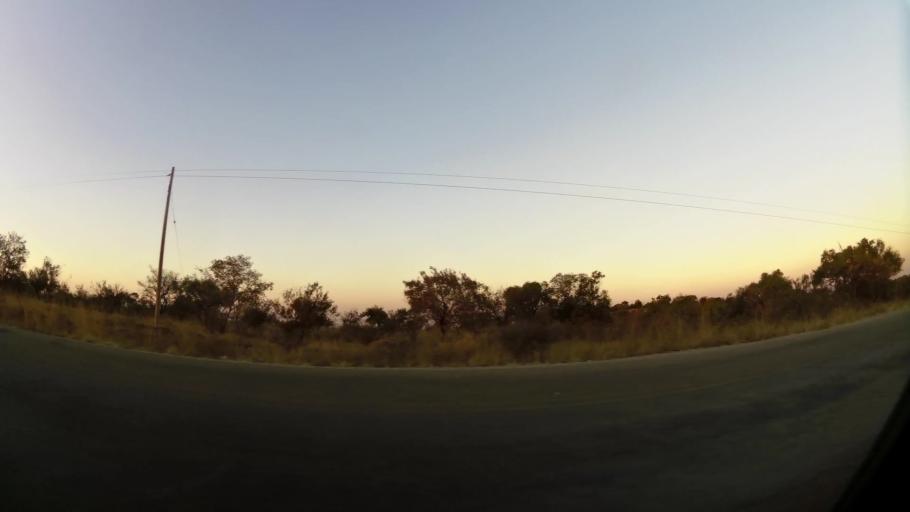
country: ZA
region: North-West
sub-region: Bojanala Platinum District Municipality
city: Rustenburg
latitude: -25.6329
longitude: 27.1932
